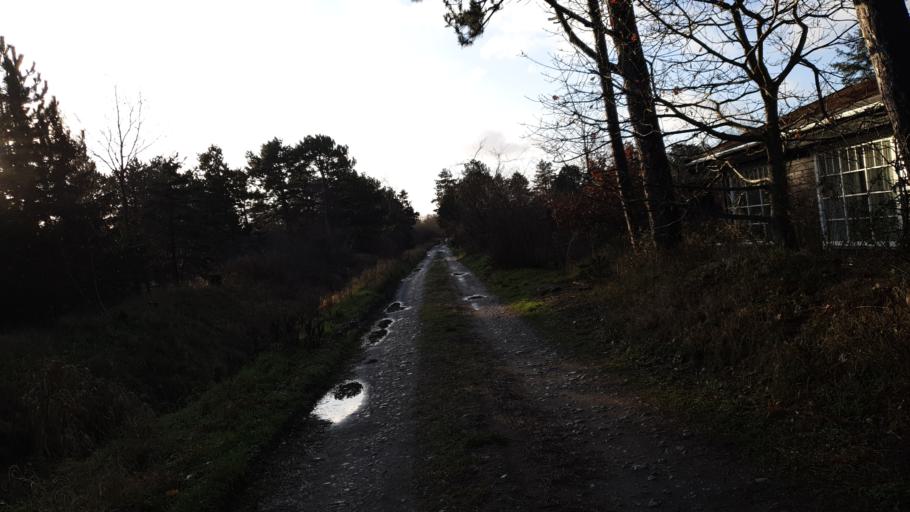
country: DK
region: Zealand
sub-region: Odsherred Kommune
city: Nykobing Sjaelland
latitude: 55.9372
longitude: 11.6372
